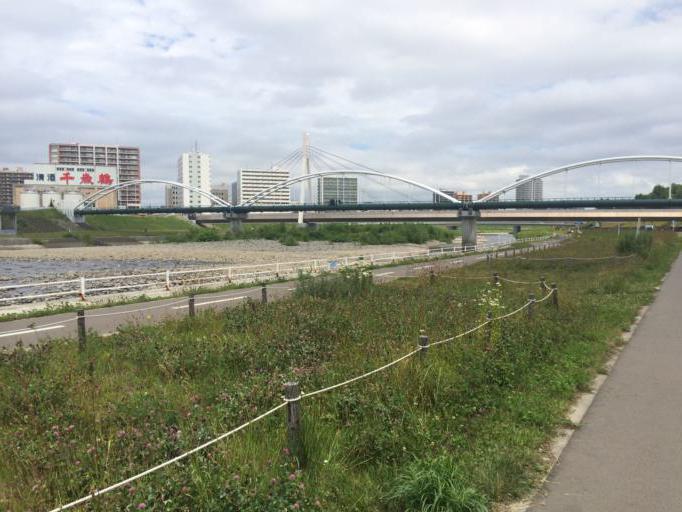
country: JP
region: Hokkaido
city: Sapporo
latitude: 43.0566
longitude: 141.3663
